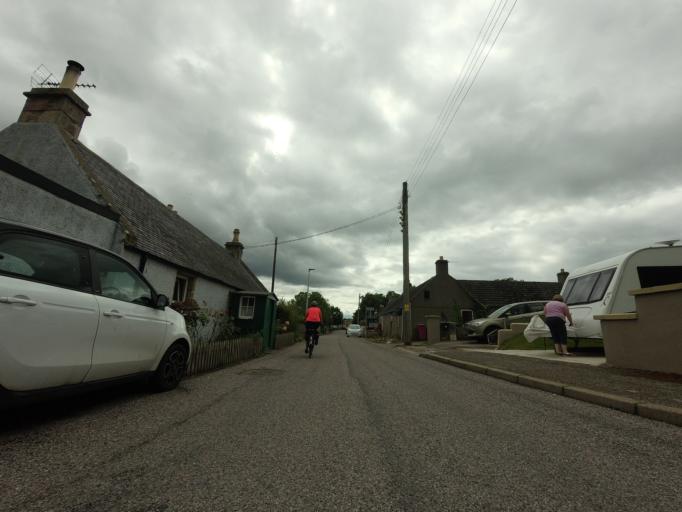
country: GB
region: Scotland
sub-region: Moray
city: Forres
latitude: 57.6043
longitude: -3.6925
